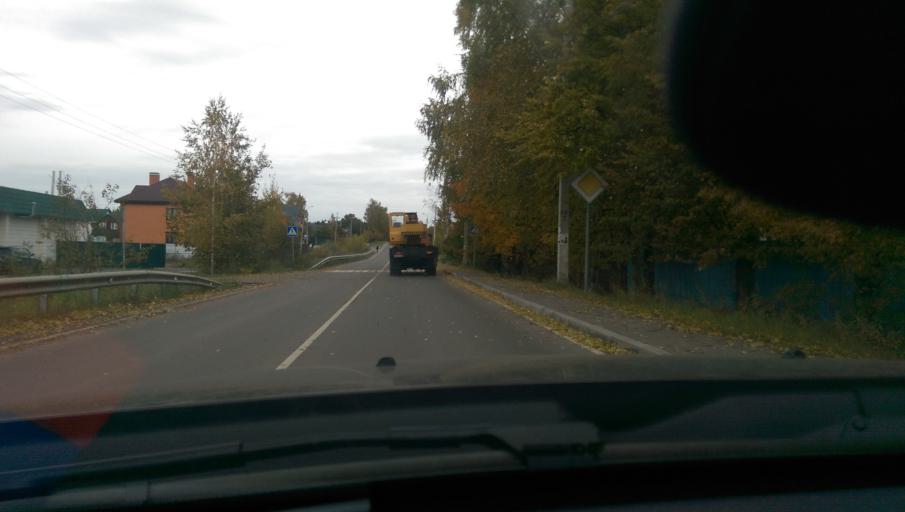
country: RU
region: Moskovskaya
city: Pirogovskiy
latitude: 56.0135
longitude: 37.7187
